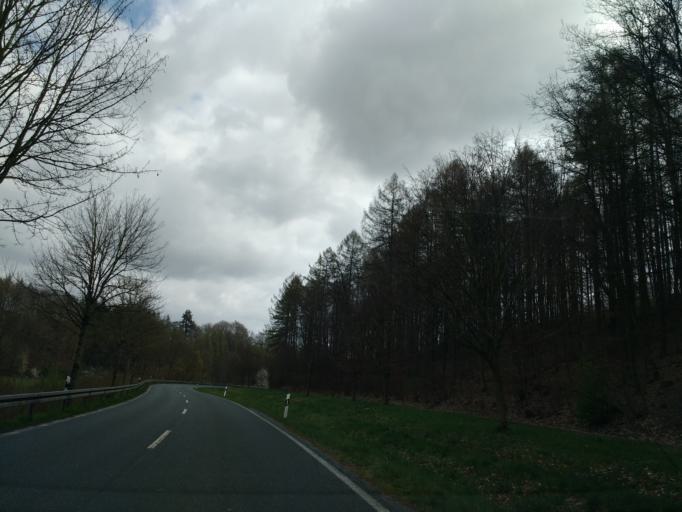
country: DE
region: North Rhine-Westphalia
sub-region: Regierungsbezirk Detmold
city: Wunnenberg
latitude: 51.5178
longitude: 8.7264
